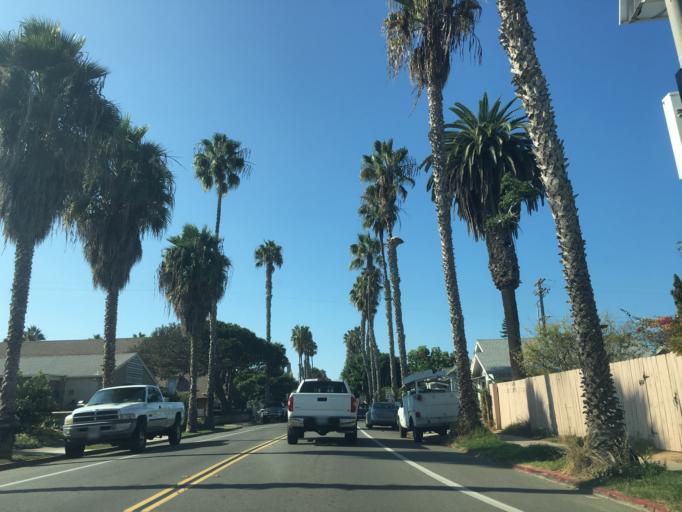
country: US
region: California
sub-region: San Diego County
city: Coronado
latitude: 32.7481
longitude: -117.2447
